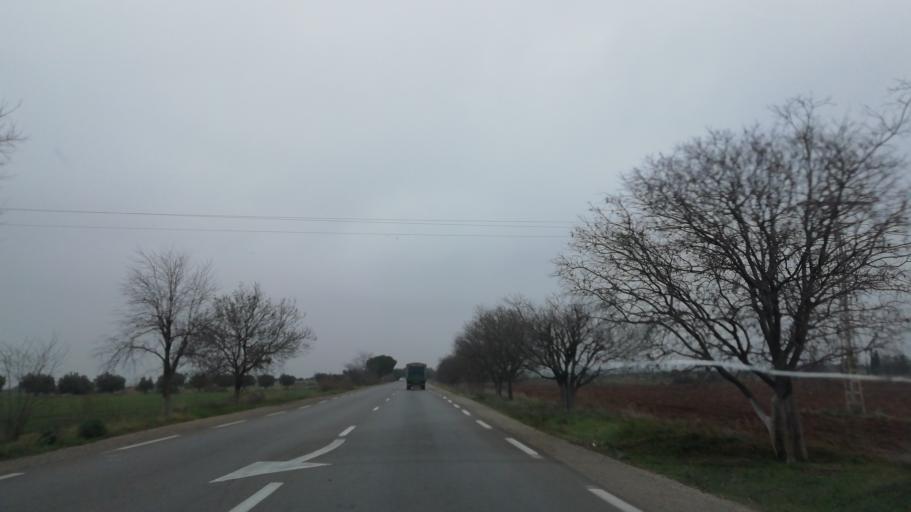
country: DZ
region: Mascara
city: Mascara
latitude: 35.3154
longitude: 0.3800
